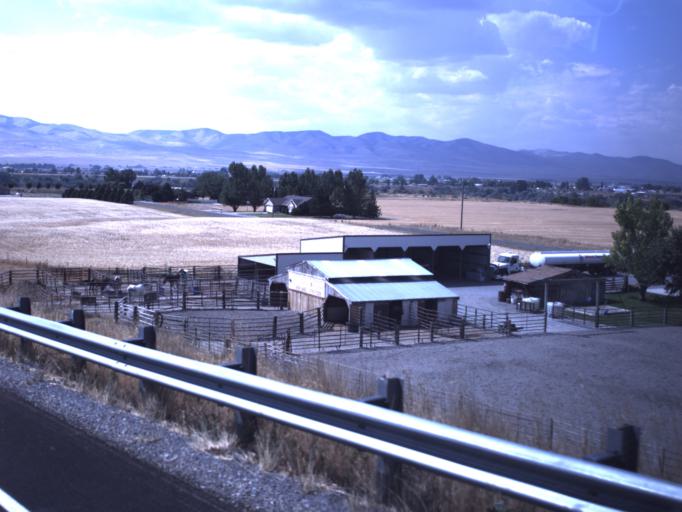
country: US
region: Utah
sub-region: Box Elder County
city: Garland
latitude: 41.7847
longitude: -112.0952
